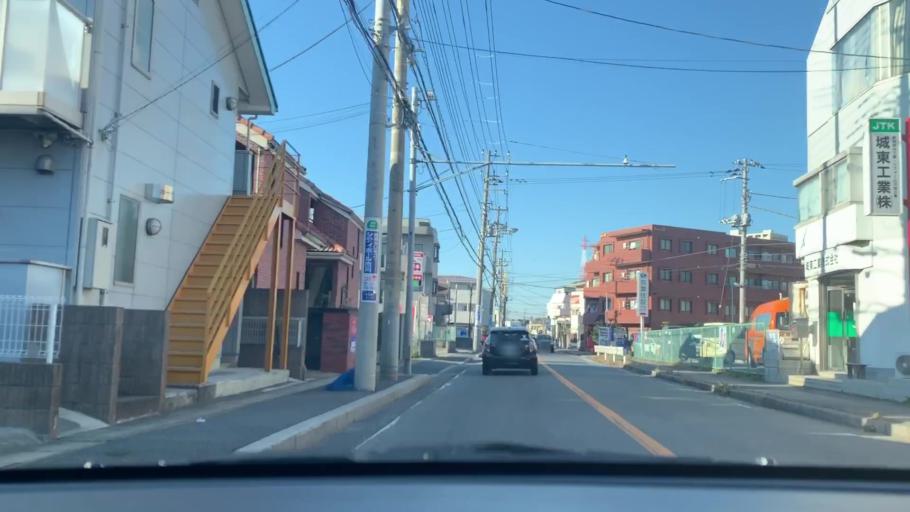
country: JP
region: Tokyo
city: Urayasu
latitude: 35.7256
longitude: 139.9020
